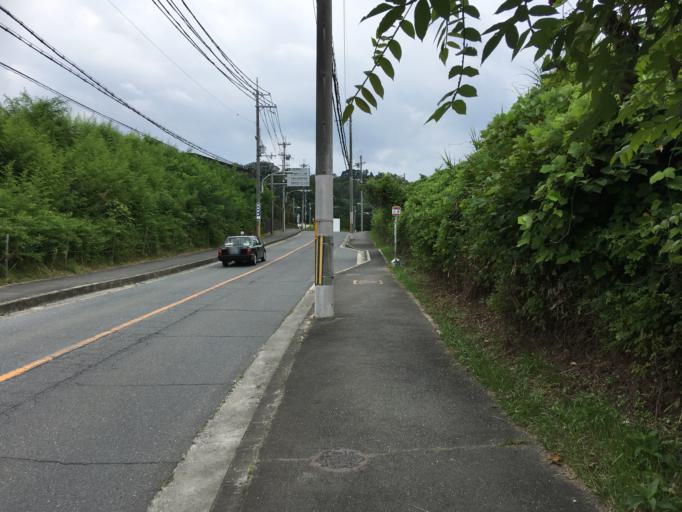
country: JP
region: Nara
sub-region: Ikoma-shi
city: Ikoma
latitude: 34.6643
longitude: 135.7178
